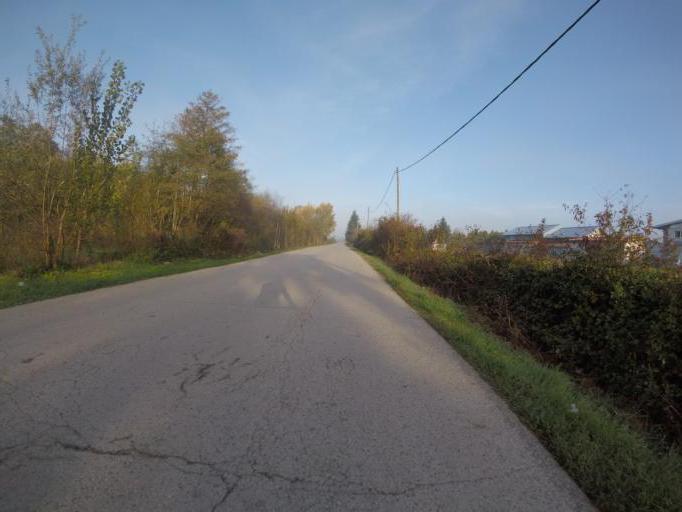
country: HR
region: Zagrebacka
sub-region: Grad Velika Gorica
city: Velika Gorica
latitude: 45.7202
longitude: 16.1207
